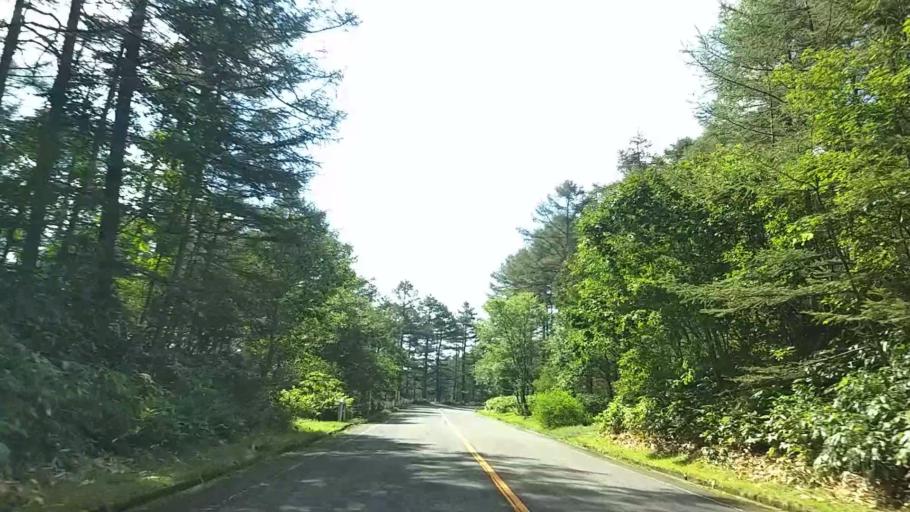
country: JP
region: Nagano
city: Suwa
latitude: 36.1485
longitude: 138.1418
